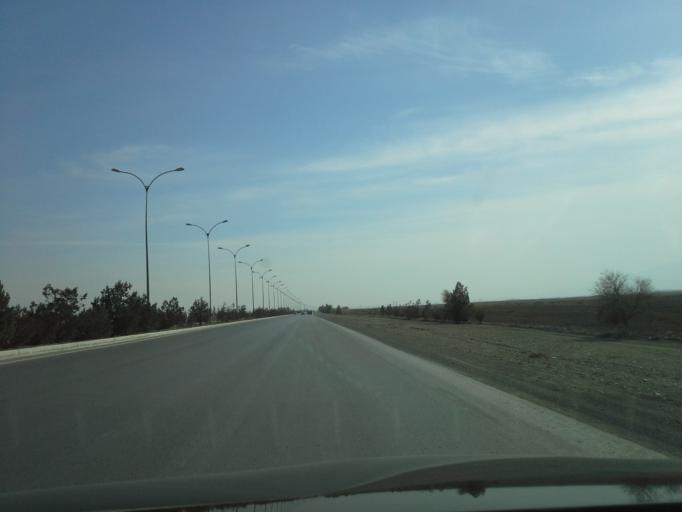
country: TM
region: Ahal
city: Abadan
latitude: 38.1293
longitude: 58.0255
